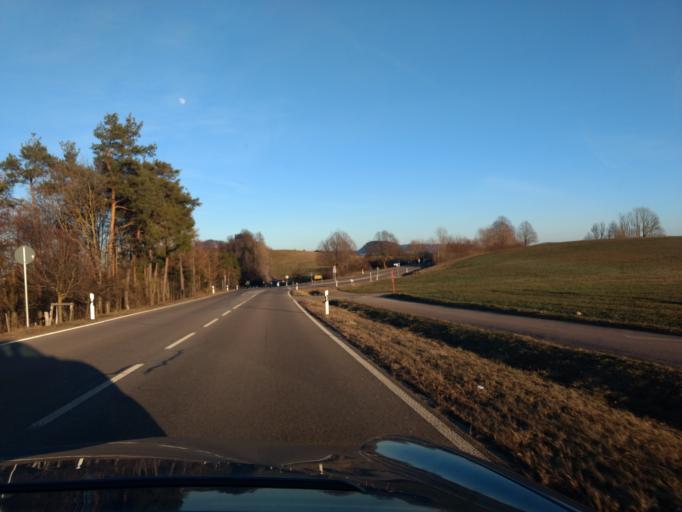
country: DE
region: Baden-Wuerttemberg
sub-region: Regierungsbezirk Stuttgart
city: Ottenbach
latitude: 48.7513
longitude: 9.7369
